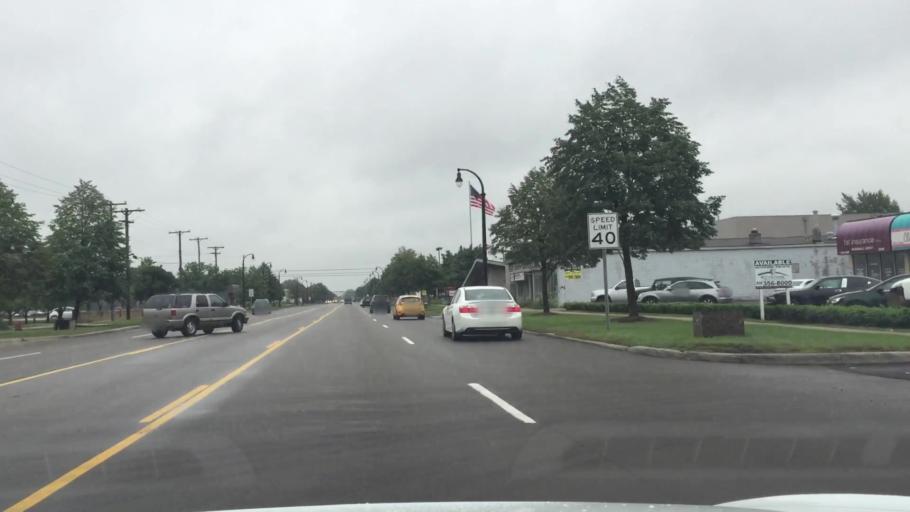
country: US
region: Michigan
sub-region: Wayne County
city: Livonia
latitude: 42.3692
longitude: -83.3316
